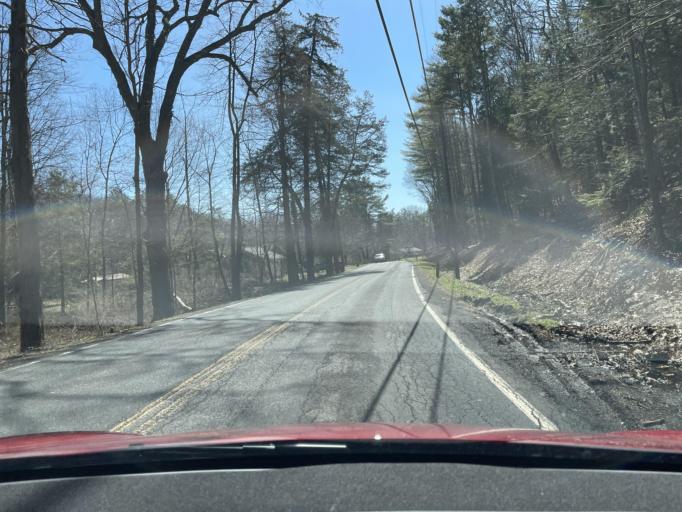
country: US
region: New York
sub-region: Ulster County
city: Saugerties South
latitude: 42.0435
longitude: -74.0053
